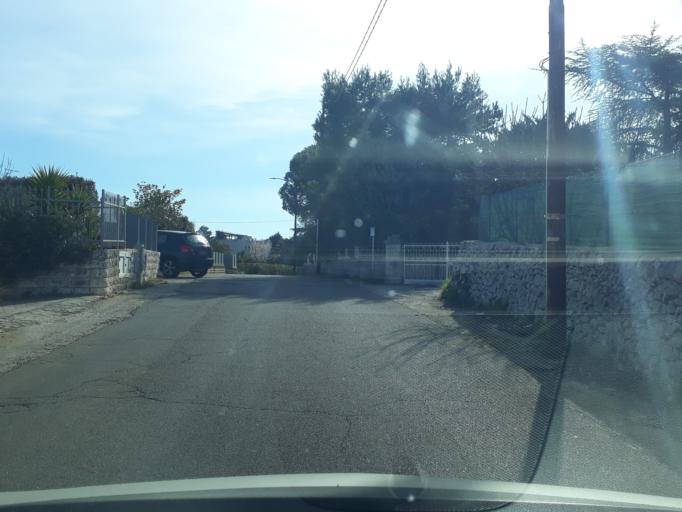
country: IT
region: Apulia
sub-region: Provincia di Brindisi
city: Lamie di Olimpie-Selva
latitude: 40.7956
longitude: 17.3516
